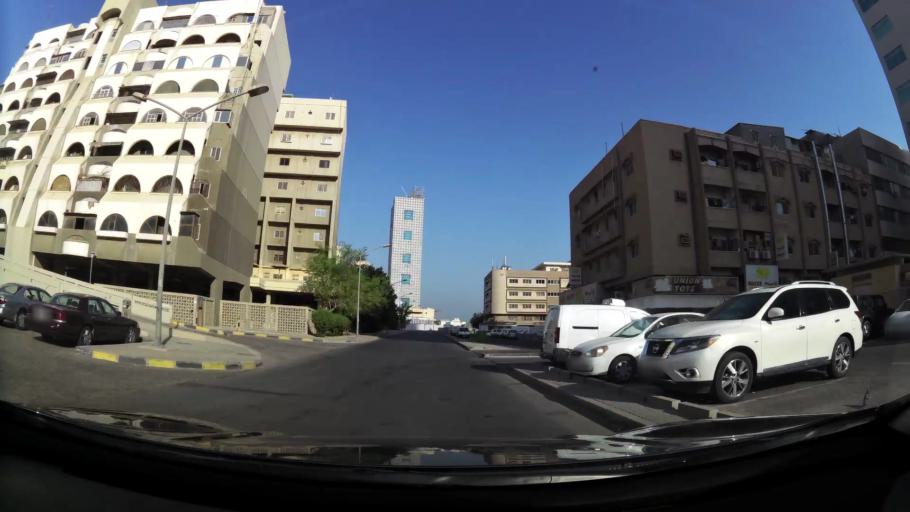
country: KW
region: Al Asimah
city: Kuwait City
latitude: 29.3768
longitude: 47.9842
